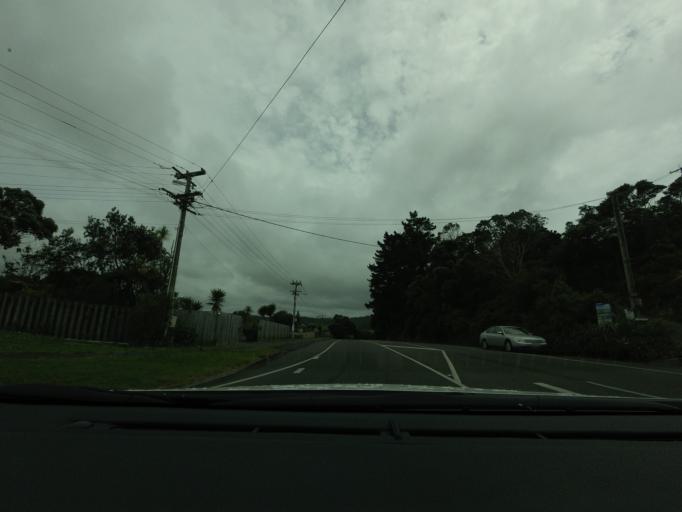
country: NZ
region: Auckland
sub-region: Auckland
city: Rothesay Bay
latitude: -36.5706
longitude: 174.6927
